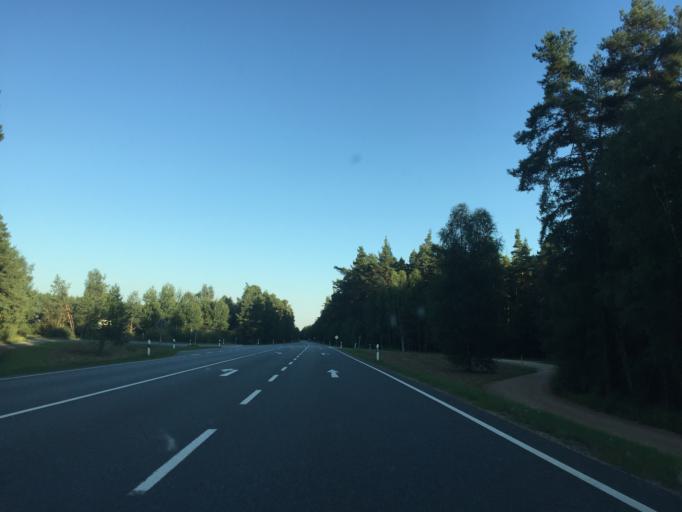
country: DE
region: Bavaria
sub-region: Upper Palatinate
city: Pressath
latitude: 49.7389
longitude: 11.9490
